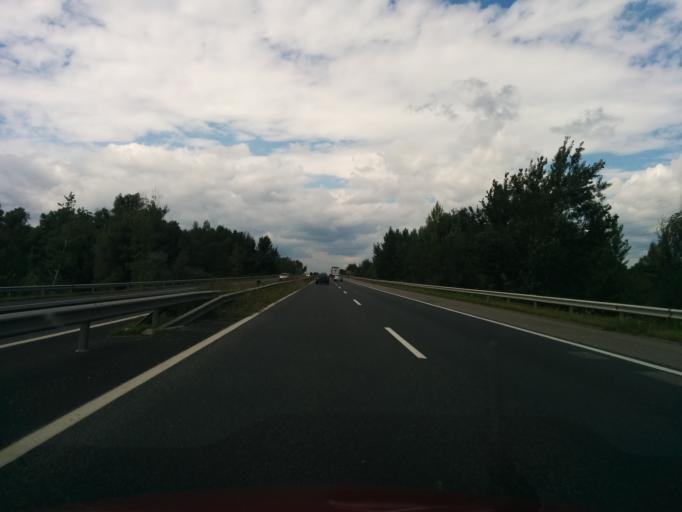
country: HU
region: Gyor-Moson-Sopron
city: Gyor
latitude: 47.6512
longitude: 17.6044
